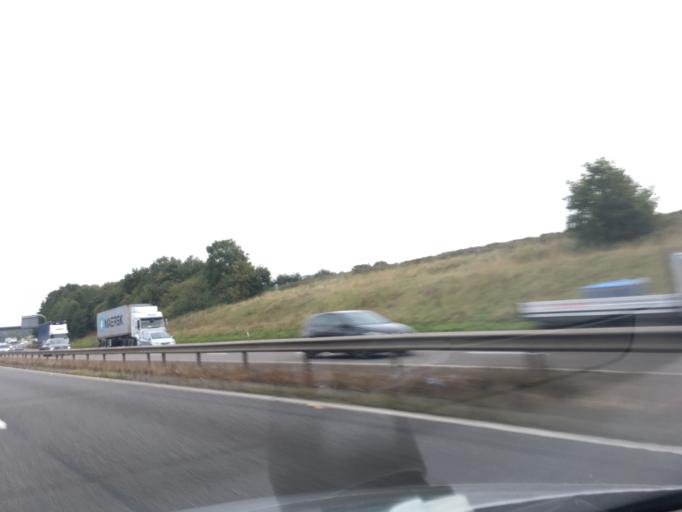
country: GB
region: England
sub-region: Oxfordshire
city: Somerton
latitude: 51.9766
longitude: -1.2626
